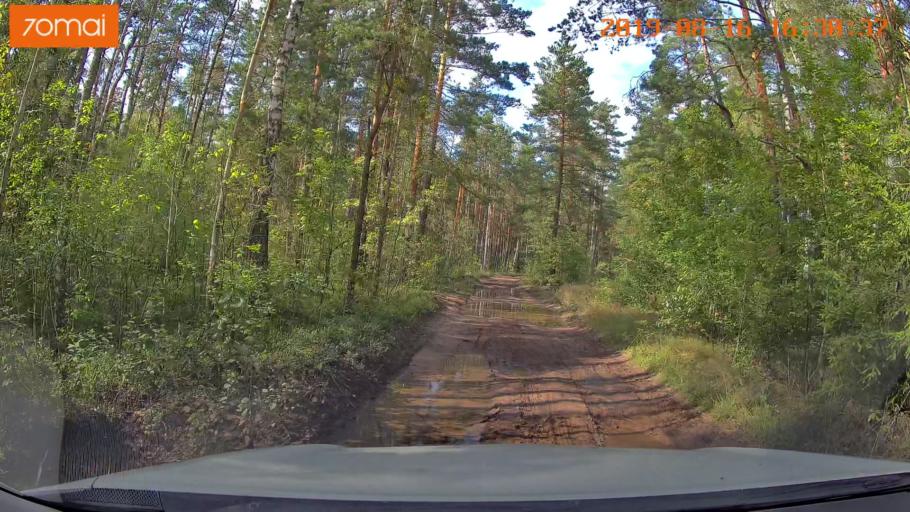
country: BY
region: Mogilev
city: Asipovichy
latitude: 53.2259
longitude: 28.7734
